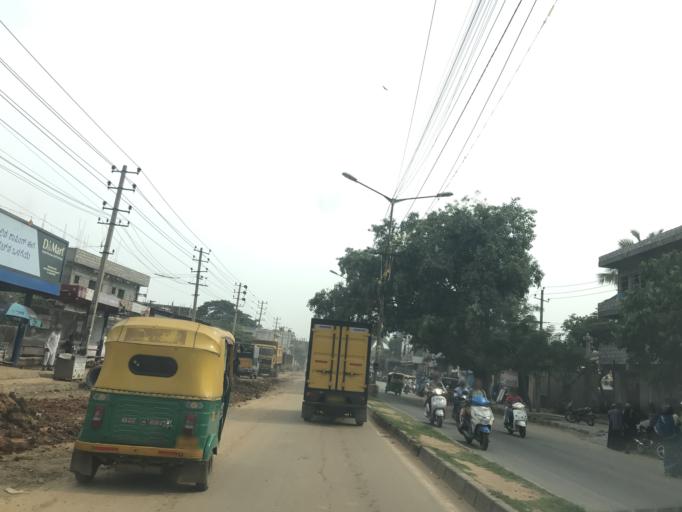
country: IN
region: Karnataka
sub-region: Bangalore Urban
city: Yelahanka
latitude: 13.0474
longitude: 77.6287
